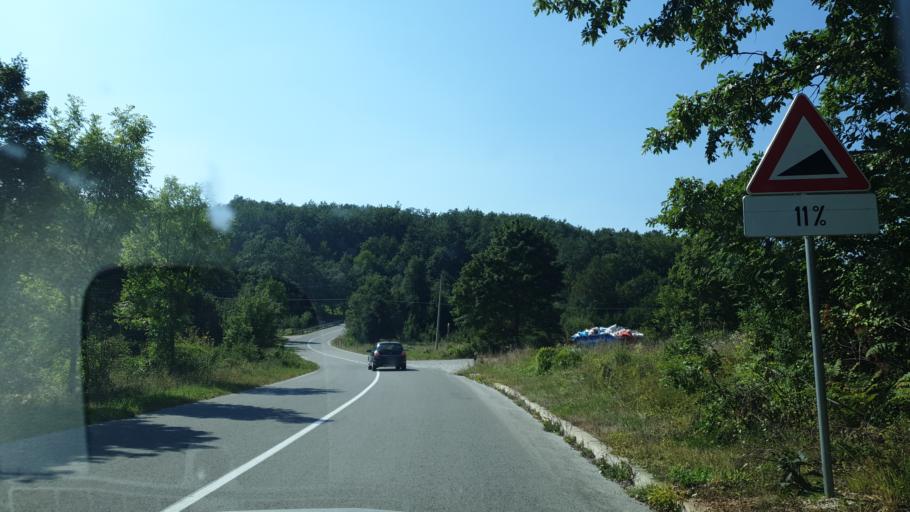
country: RS
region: Central Serbia
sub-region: Zlatiborski Okrug
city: Cajetina
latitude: 43.7190
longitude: 19.7933
